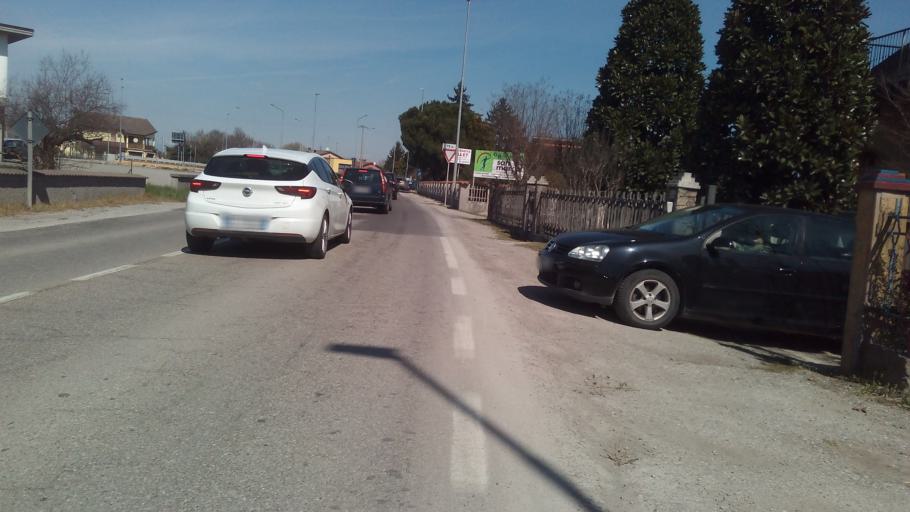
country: IT
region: Lombardy
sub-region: Provincia di Mantova
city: Goito
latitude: 45.2500
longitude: 10.6661
